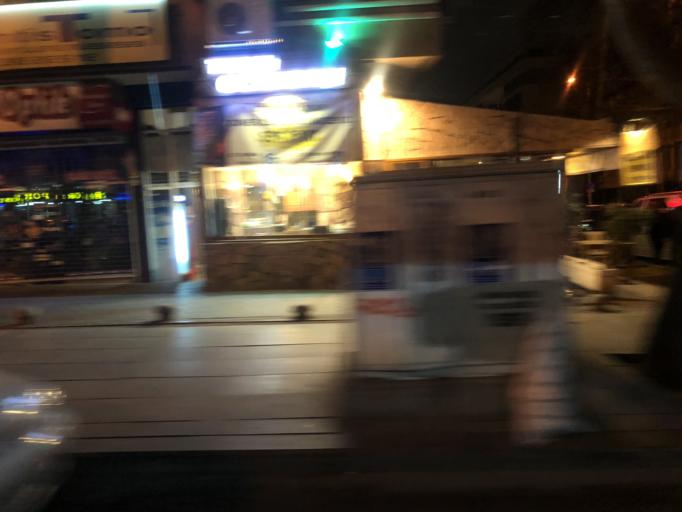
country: TR
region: Ankara
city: Cankaya
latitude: 39.9199
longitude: 32.8590
